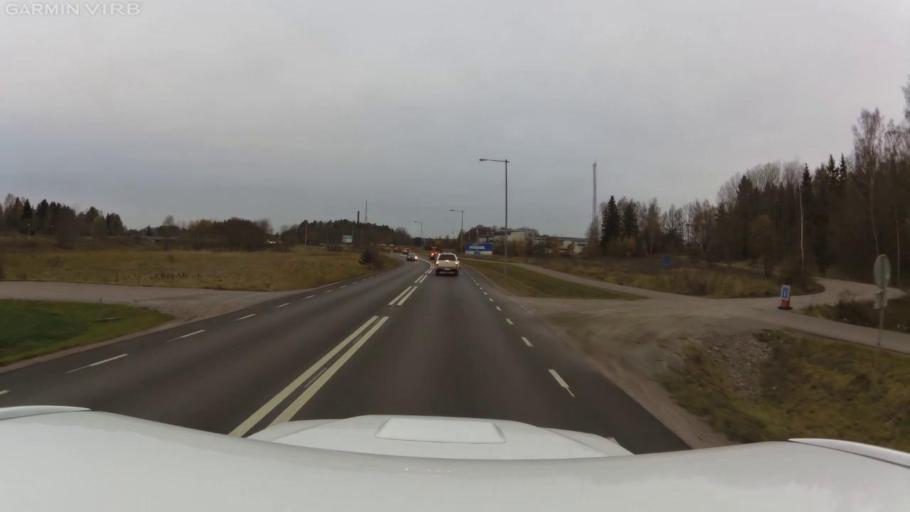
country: SE
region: OEstergoetland
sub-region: Linkopings Kommun
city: Linkoping
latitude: 58.3889
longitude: 15.5855
